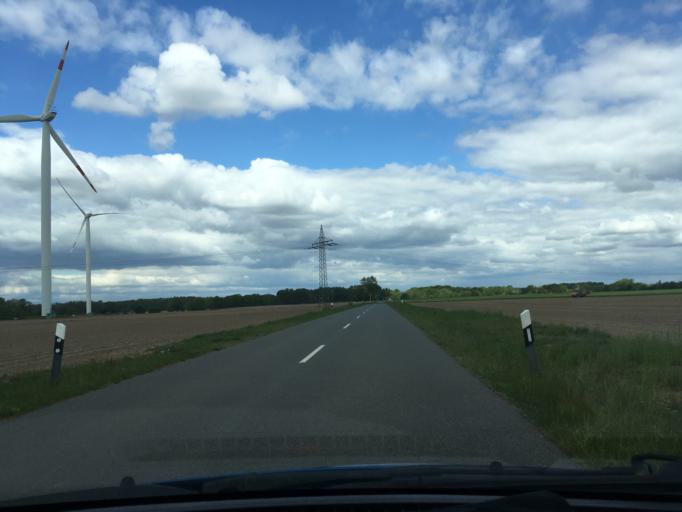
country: DE
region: Lower Saxony
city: Suderburg
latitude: 52.9149
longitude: 10.4397
